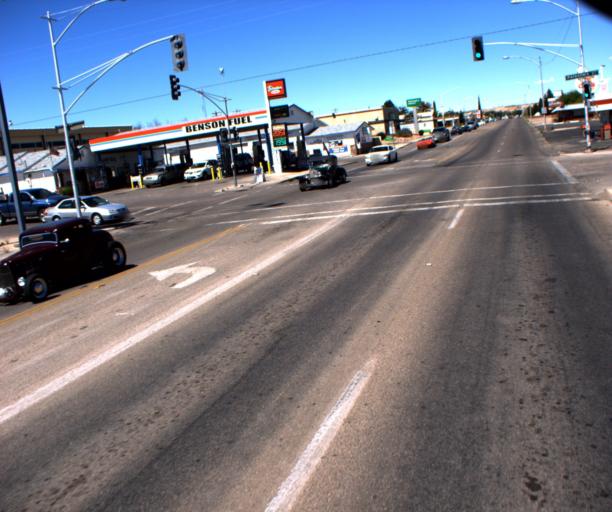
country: US
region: Arizona
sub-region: Cochise County
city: Benson
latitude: 31.9685
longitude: -110.2971
